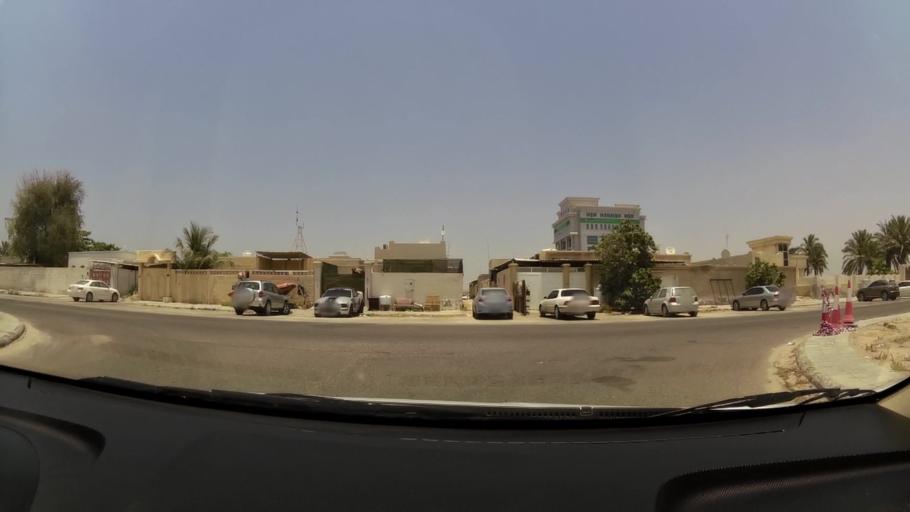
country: AE
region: Umm al Qaywayn
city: Umm al Qaywayn
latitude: 25.5516
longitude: 55.5453
